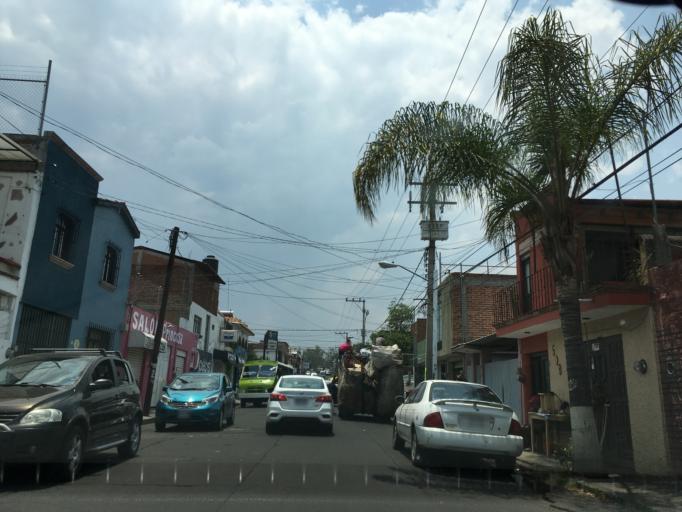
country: MX
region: Michoacan
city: Morelia
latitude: 19.6923
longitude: -101.2021
